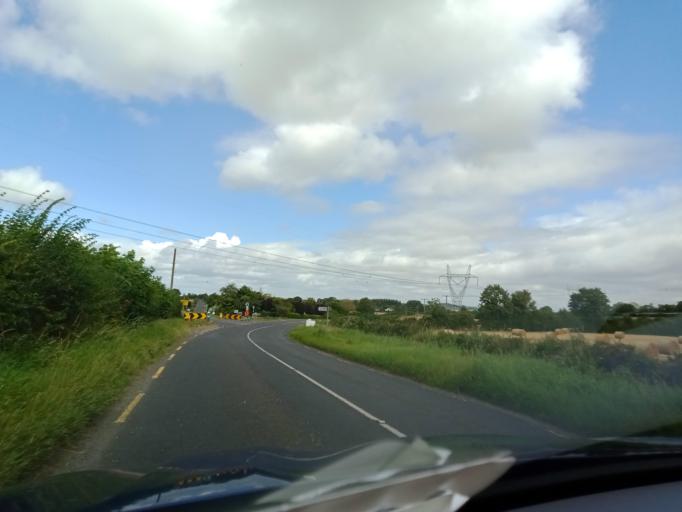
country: IE
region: Leinster
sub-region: Laois
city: Portlaoise
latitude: 52.9714
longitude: -7.2934
